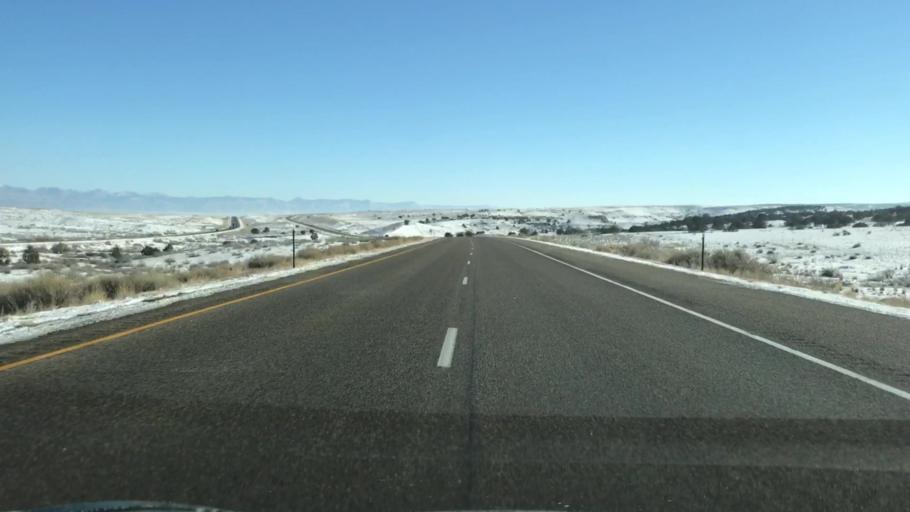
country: US
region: Colorado
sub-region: Mesa County
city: Loma
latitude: 39.2211
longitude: -108.9508
